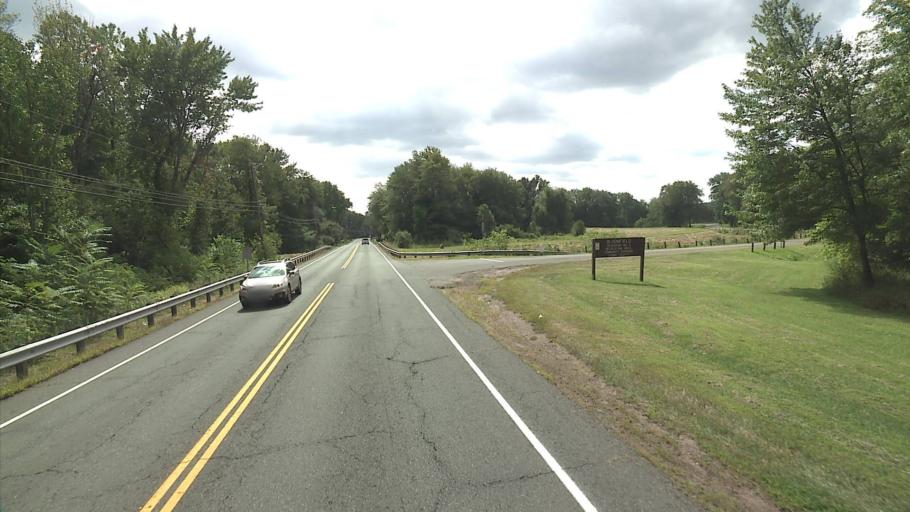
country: US
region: Connecticut
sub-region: Hartford County
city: Tariffville
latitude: 41.8627
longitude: -72.7424
